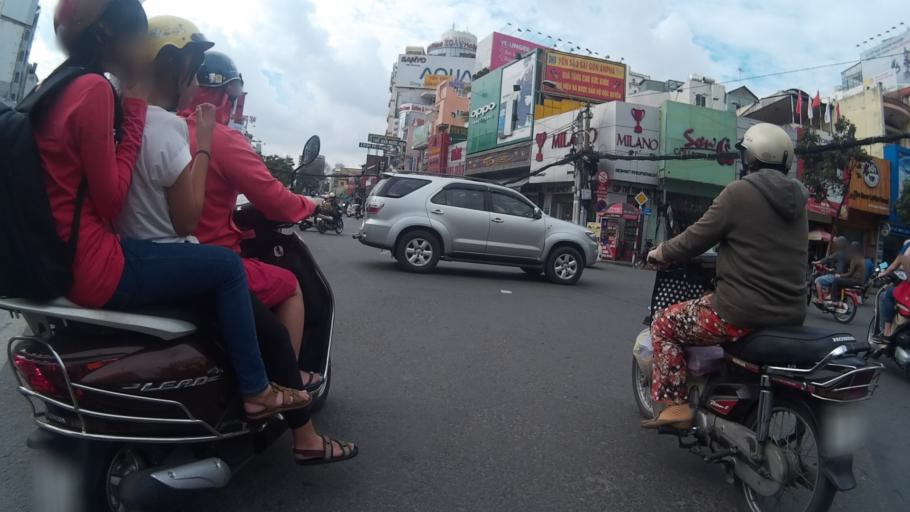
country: VN
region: Ho Chi Minh City
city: Quan Ba
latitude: 10.7712
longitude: 106.6936
